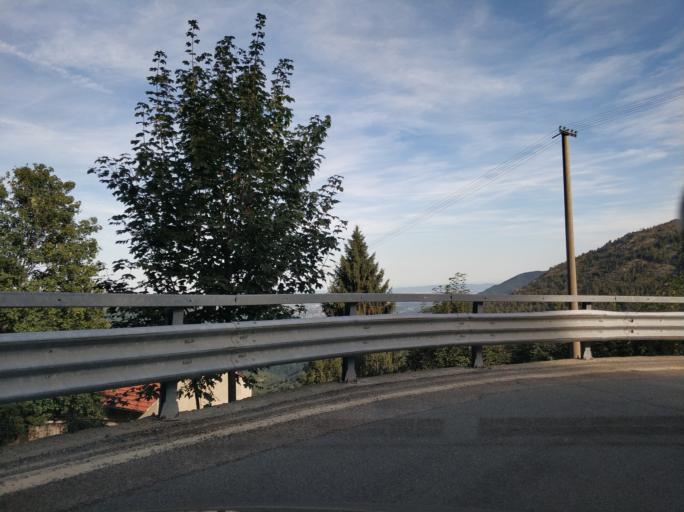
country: IT
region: Piedmont
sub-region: Provincia di Torino
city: Monastero di Lanzo
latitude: 45.3034
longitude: 7.4302
